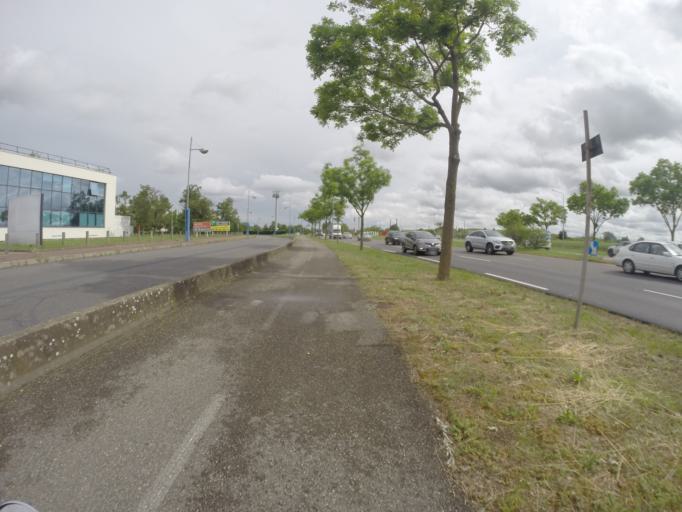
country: FR
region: Rhone-Alpes
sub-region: Departement du Rhone
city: Bron
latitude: 45.7378
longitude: 4.9349
